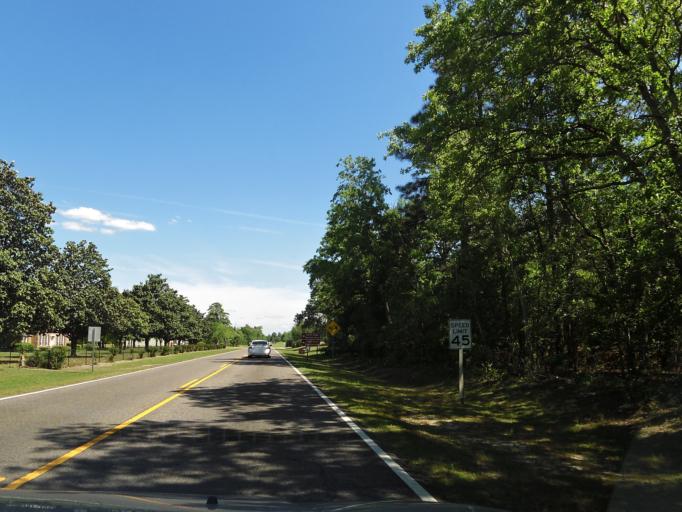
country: US
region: South Carolina
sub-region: Barnwell County
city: Williston
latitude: 33.4870
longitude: -81.5194
